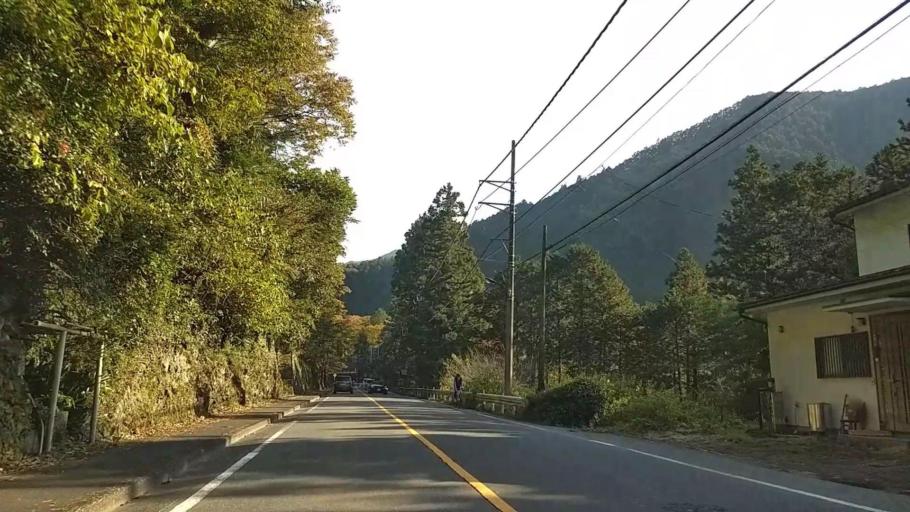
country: JP
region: Tokyo
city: Ome
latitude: 35.8073
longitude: 139.1699
